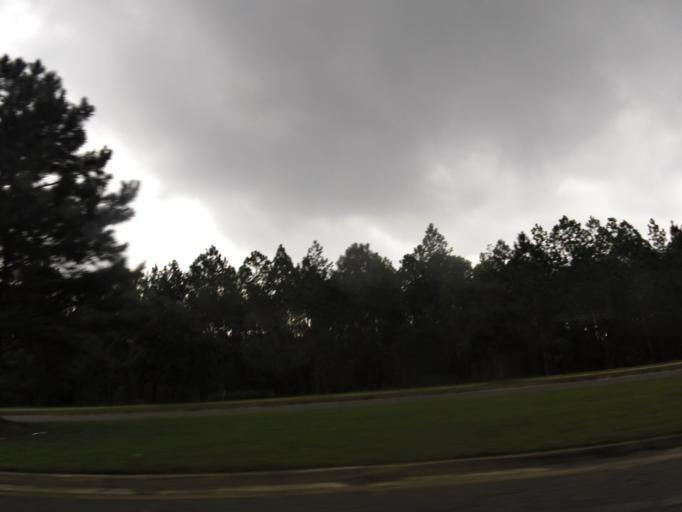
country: US
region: Florida
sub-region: Clay County
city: Lakeside
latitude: 30.1867
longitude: -81.8448
